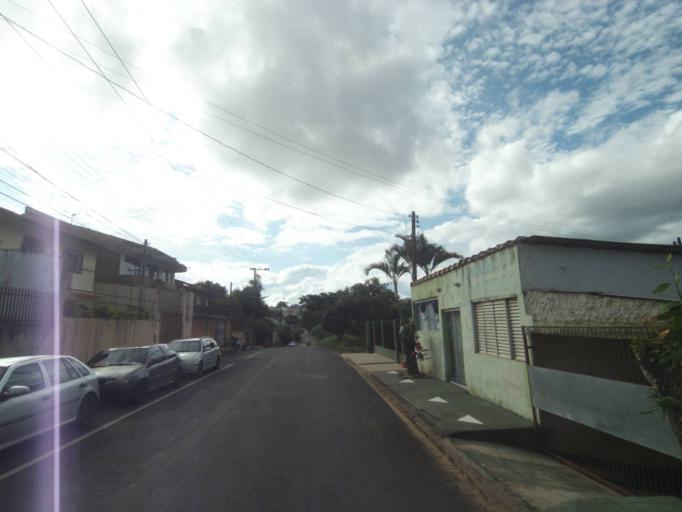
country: BR
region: Parana
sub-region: Telemaco Borba
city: Telemaco Borba
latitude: -24.3361
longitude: -50.6098
